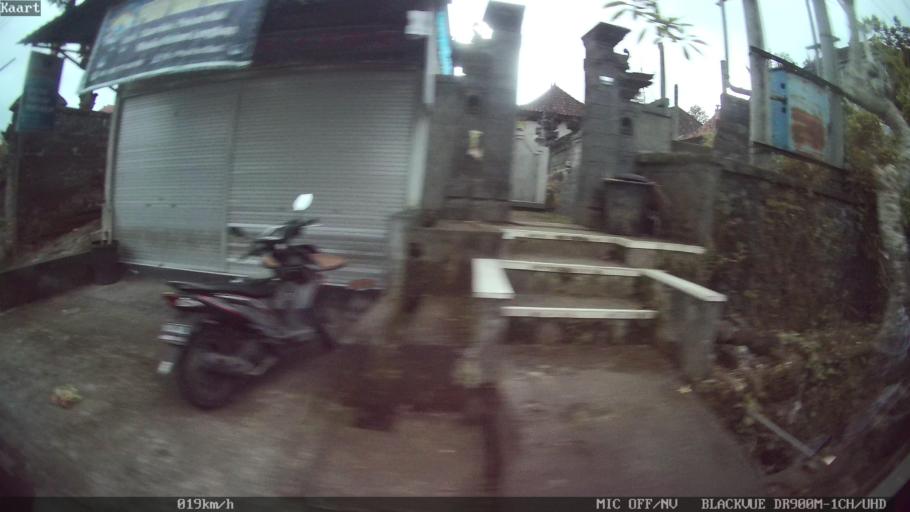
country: ID
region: Bali
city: Banjar Triwangsakeliki
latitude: -8.4487
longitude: 115.2625
